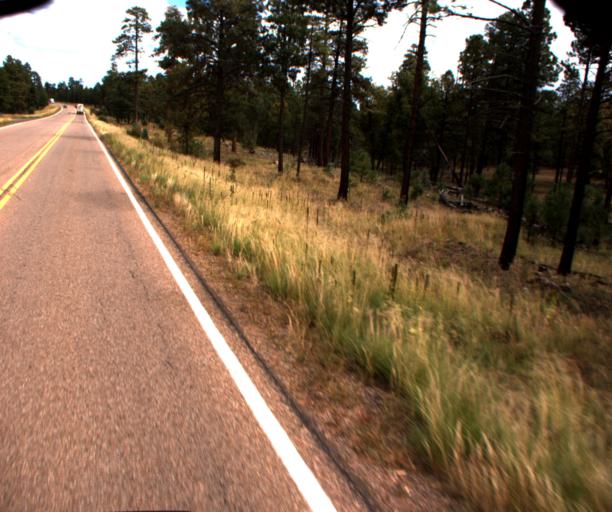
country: US
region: Arizona
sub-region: Navajo County
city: Heber-Overgaard
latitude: 34.3728
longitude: -110.6808
